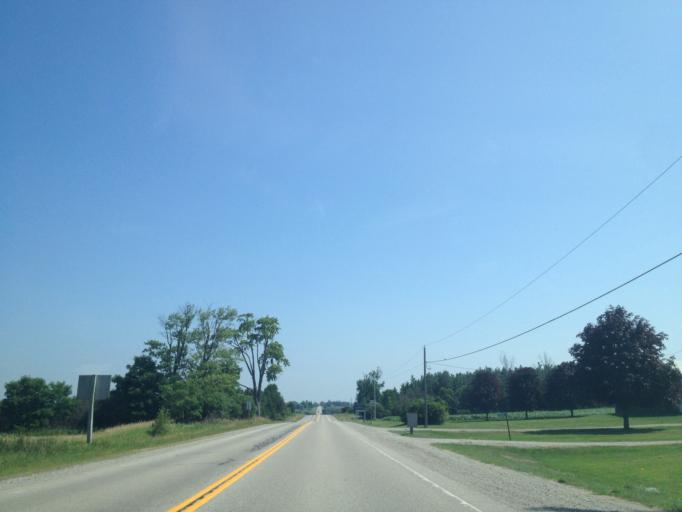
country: CA
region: Ontario
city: London
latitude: 43.2133
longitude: -81.2429
